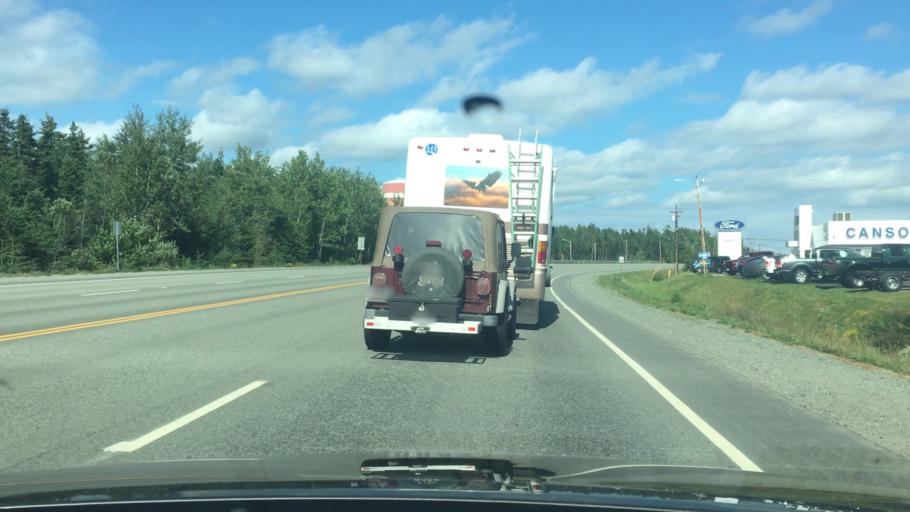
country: CA
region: Nova Scotia
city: Port Hawkesbury
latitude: 45.6140
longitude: -61.3422
